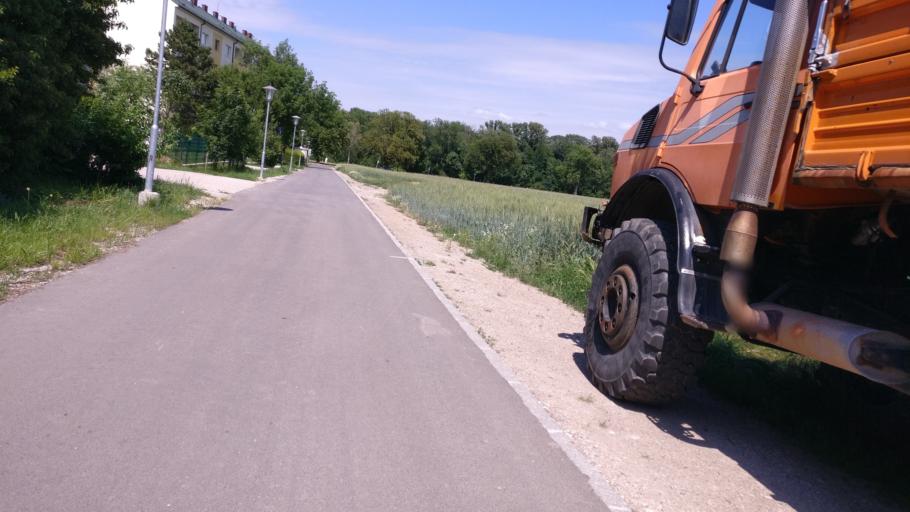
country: AT
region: Lower Austria
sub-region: Politischer Bezirk Baden
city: Gunselsdorf
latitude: 47.9443
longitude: 16.2650
